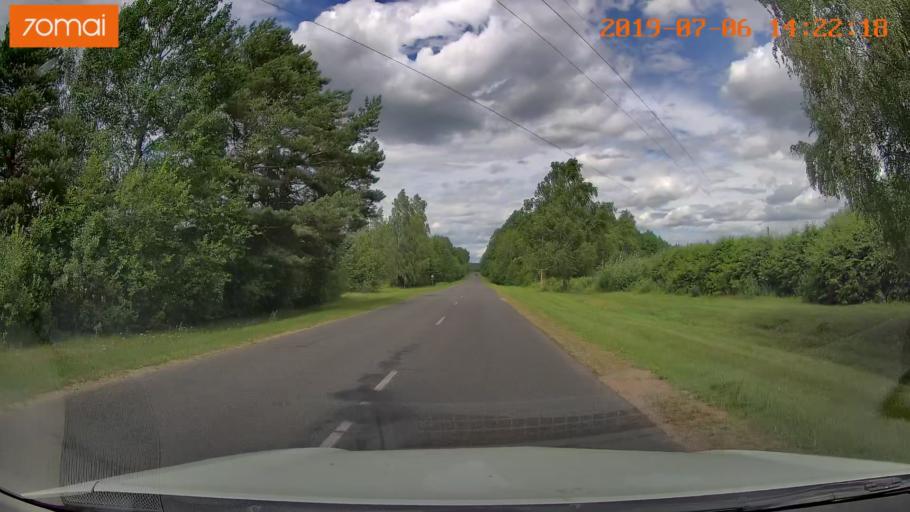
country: BY
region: Minsk
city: Ivyanyets
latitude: 53.9068
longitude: 26.7624
